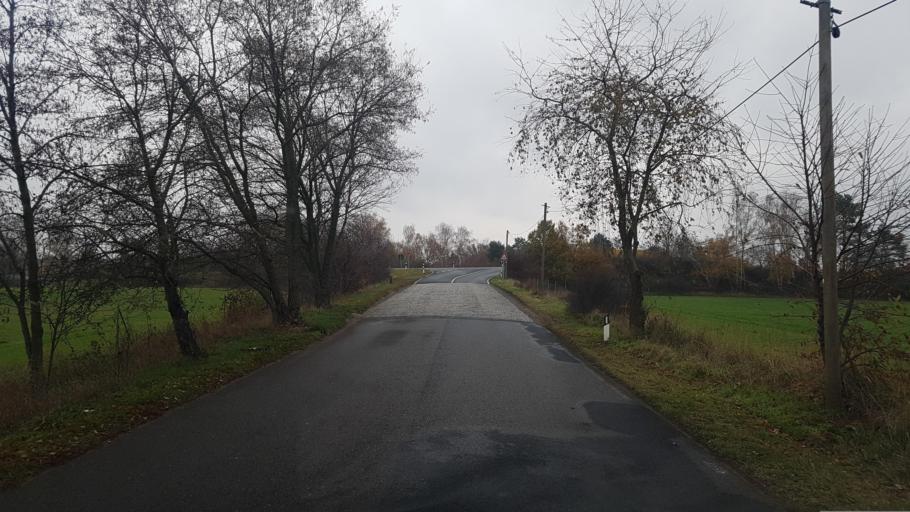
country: DE
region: Brandenburg
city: Lubbenau
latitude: 51.8327
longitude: 13.9099
